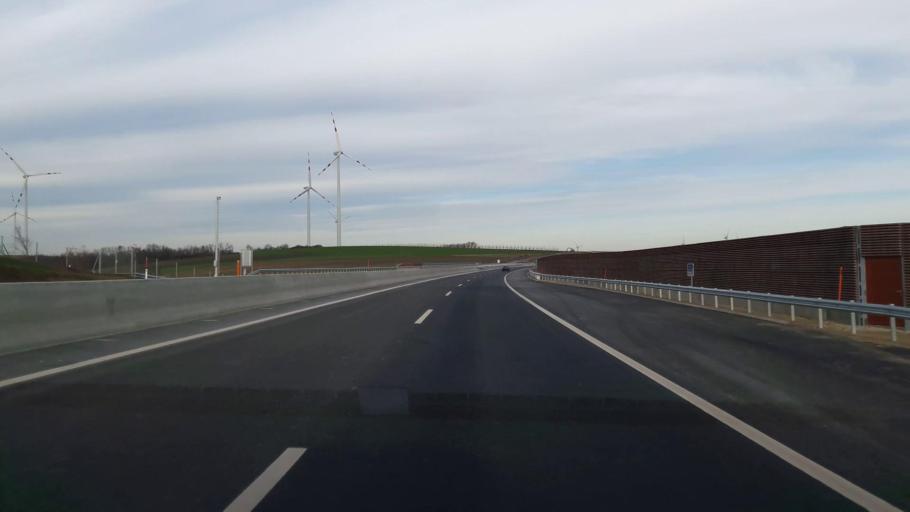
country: AT
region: Lower Austria
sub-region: Politischer Bezirk Mistelbach
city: Wilfersdorf
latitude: 48.5956
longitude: 16.6323
